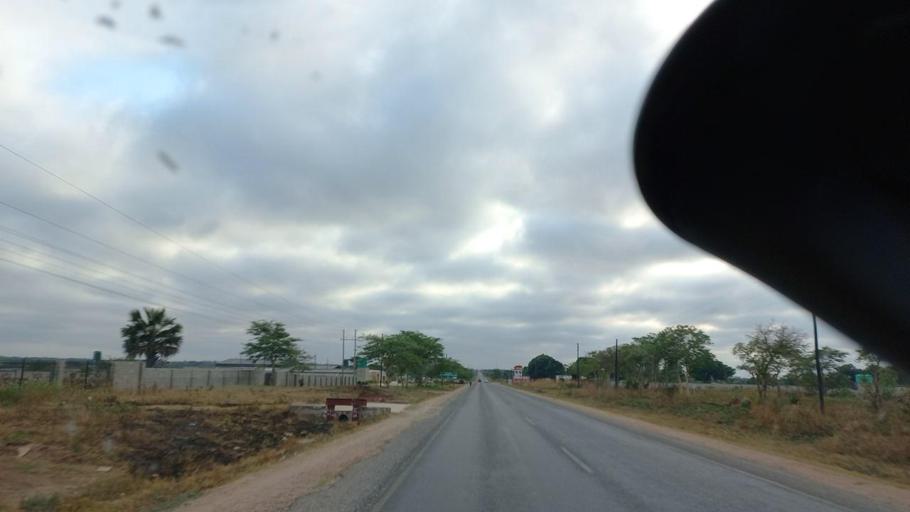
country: ZM
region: Lusaka
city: Chongwe
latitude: -15.3537
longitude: 28.4867
